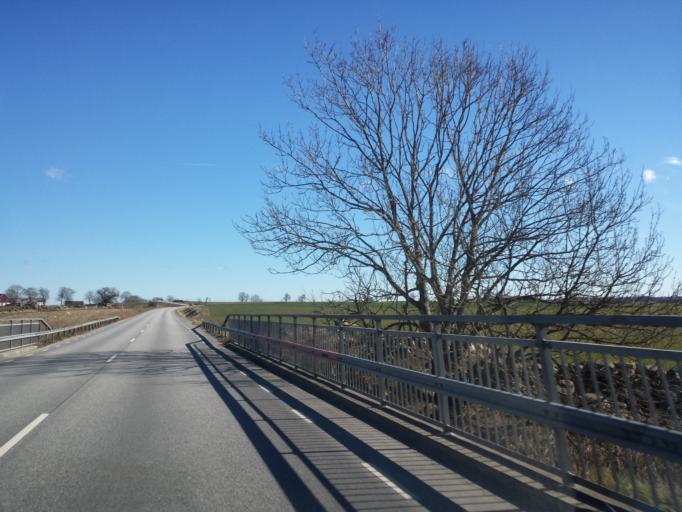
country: SE
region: Skane
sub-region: Tomelilla Kommun
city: Tomelilla
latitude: 55.6316
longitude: 13.8680
